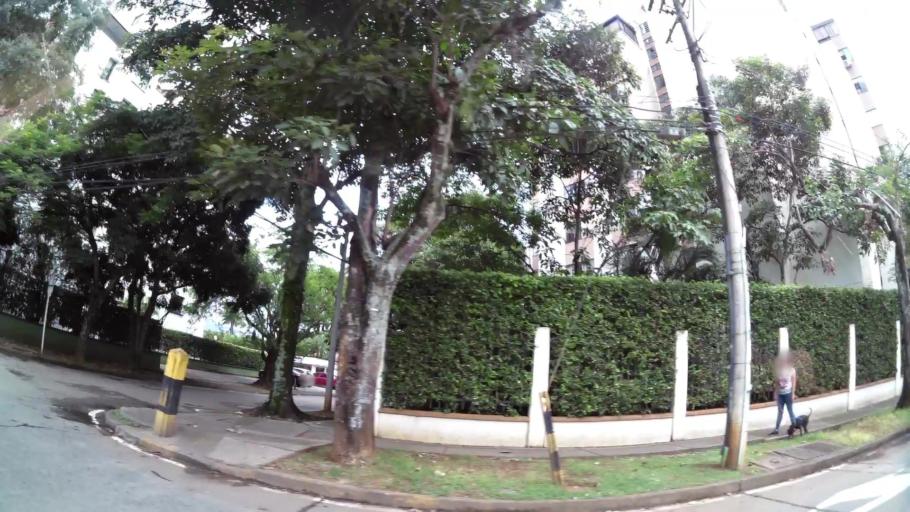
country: CO
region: Valle del Cauca
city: Cali
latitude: 3.3961
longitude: -76.5350
